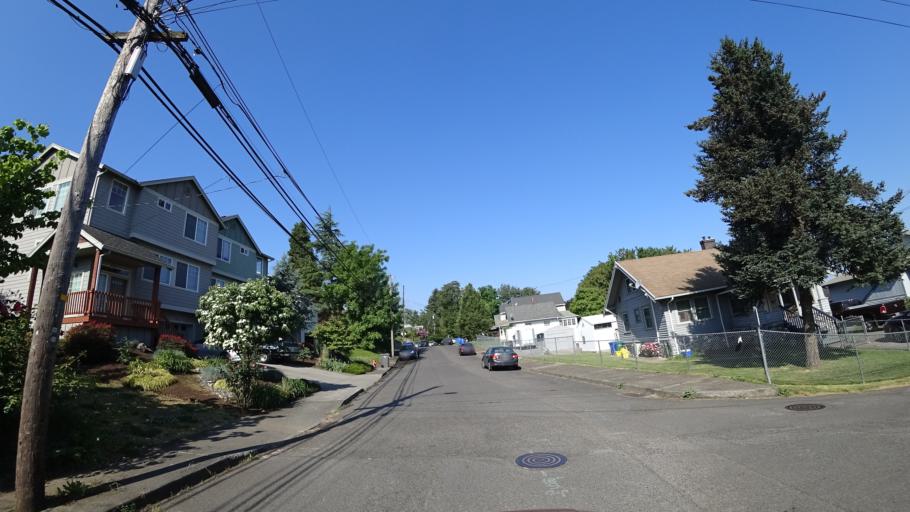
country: US
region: Oregon
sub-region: Multnomah County
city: Portland
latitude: 45.5766
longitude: -122.6548
